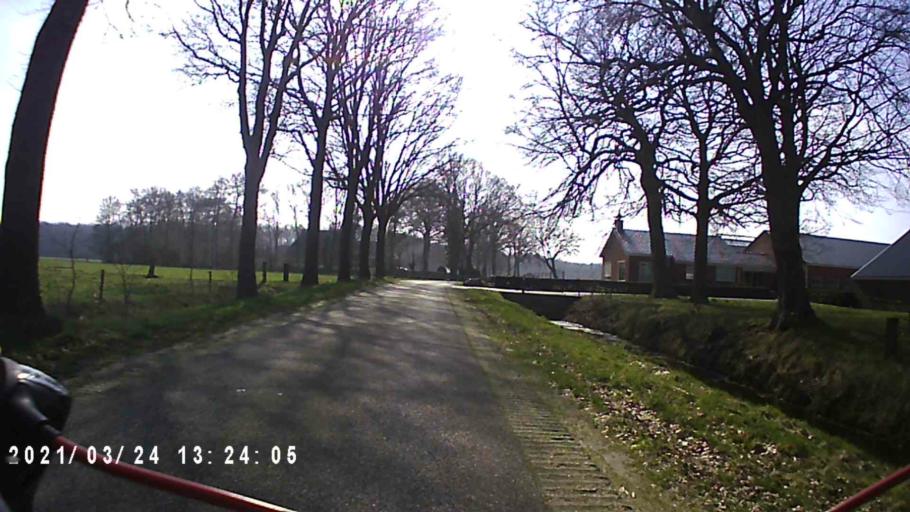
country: NL
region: Groningen
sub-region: Gemeente Grootegast
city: Grootegast
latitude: 53.0975
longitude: 6.2770
